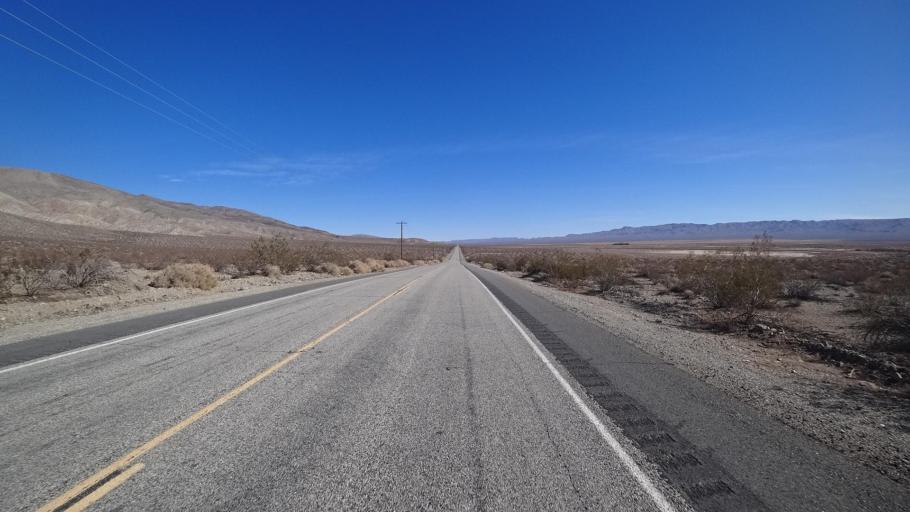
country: US
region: California
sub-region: Kern County
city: Inyokern
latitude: 35.3793
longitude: -117.8588
